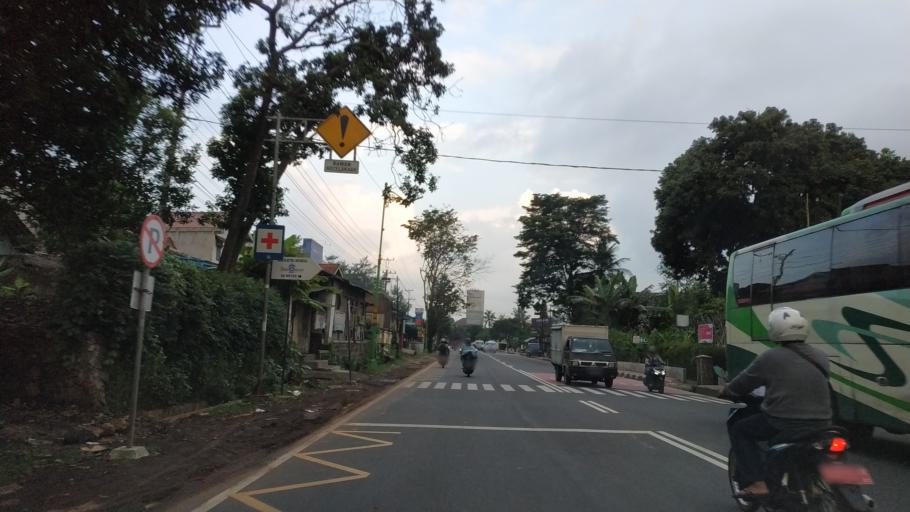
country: ID
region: Central Java
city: Salatiga
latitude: -7.3115
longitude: 110.4912
